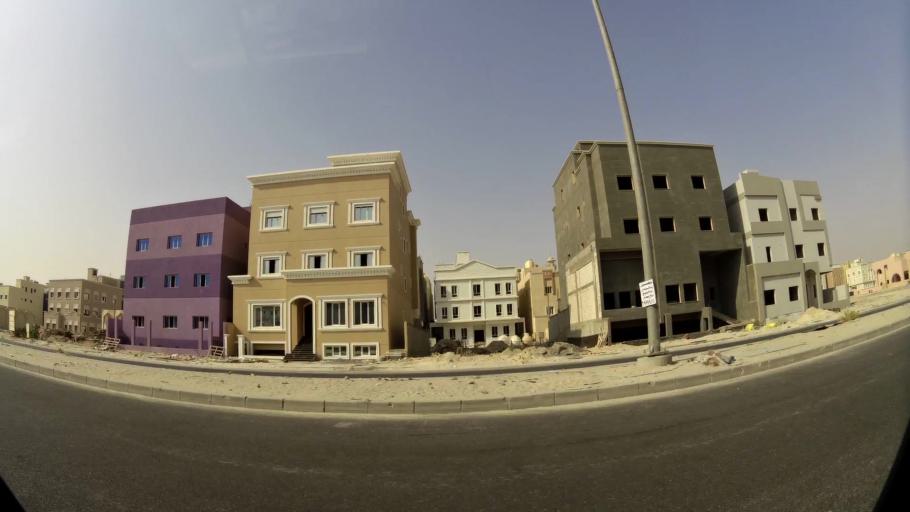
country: KW
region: Muhafazat al Jahra'
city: Al Jahra'
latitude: 29.3489
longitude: 47.7723
